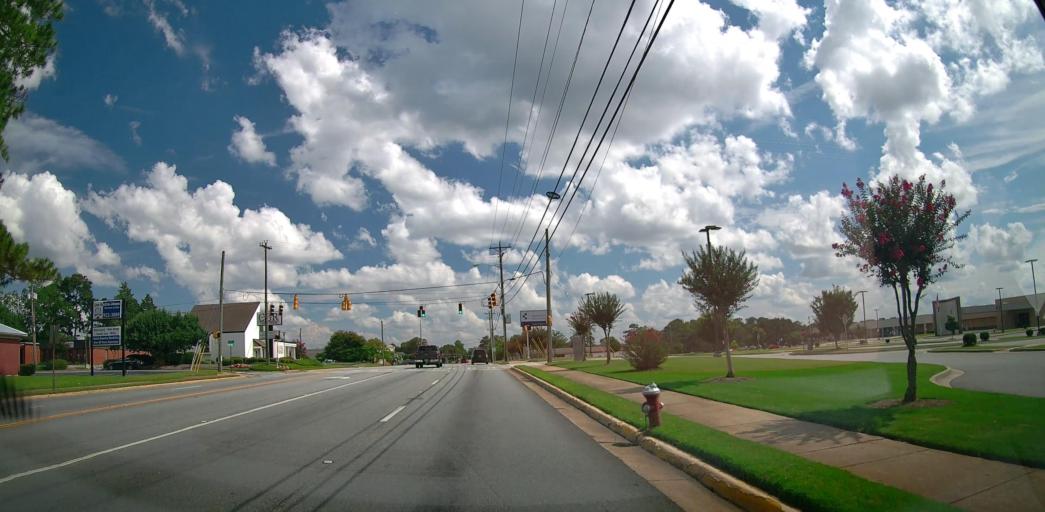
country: US
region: Georgia
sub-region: Houston County
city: Warner Robins
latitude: 32.6210
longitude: -83.6416
